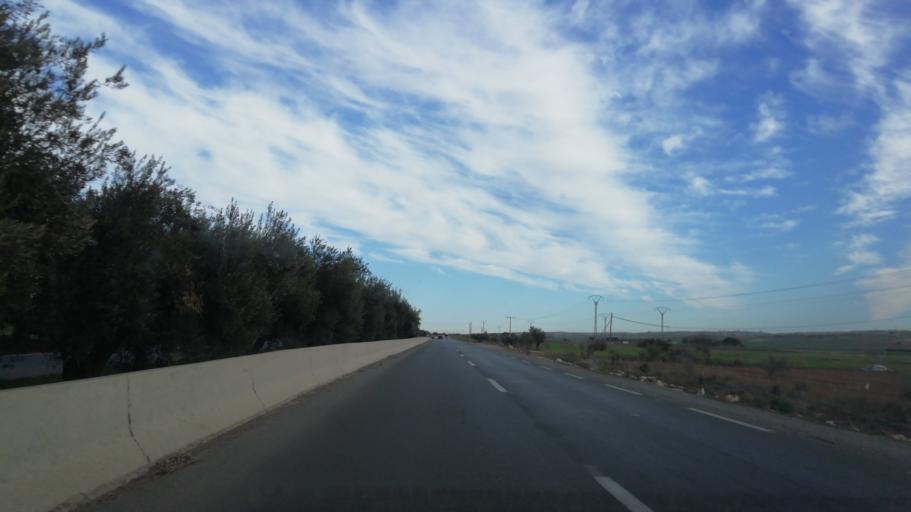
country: DZ
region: Sidi Bel Abbes
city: Sfizef
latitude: 35.1792
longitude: -0.4234
